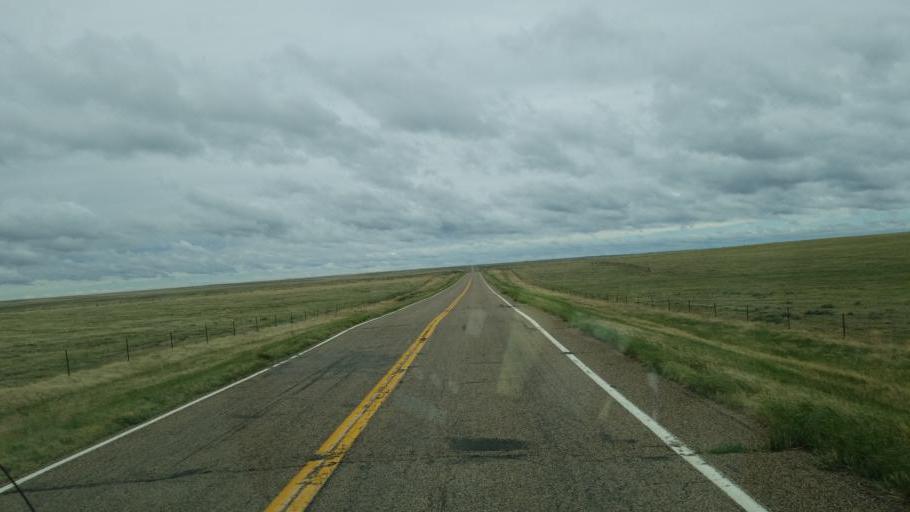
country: US
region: Colorado
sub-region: Lincoln County
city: Hugo
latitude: 38.8506
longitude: -103.5223
